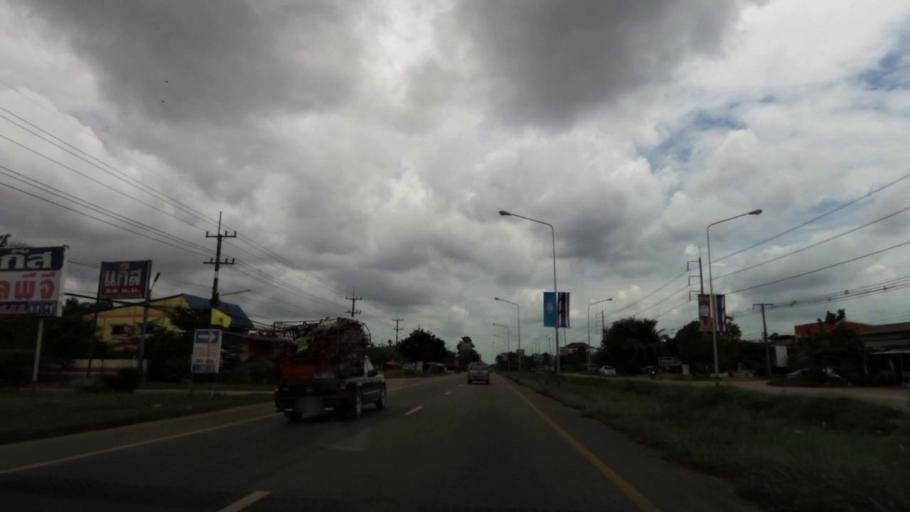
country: TH
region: Rayong
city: Klaeng
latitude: 12.7803
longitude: 101.6986
